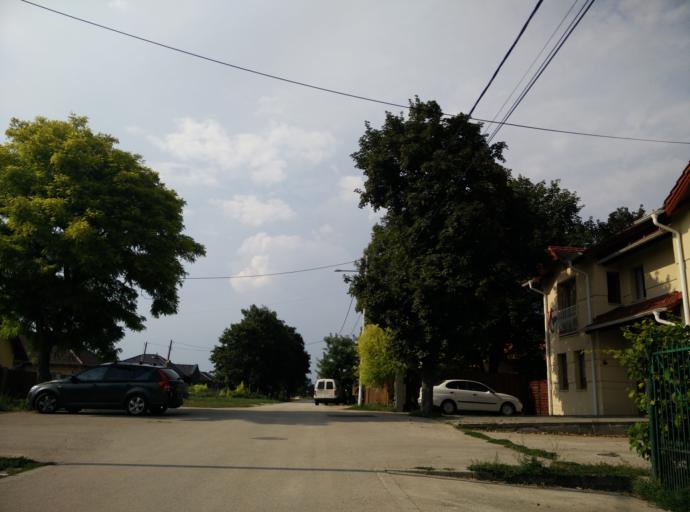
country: HU
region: Pest
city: Paty
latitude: 47.5191
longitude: 18.8236
